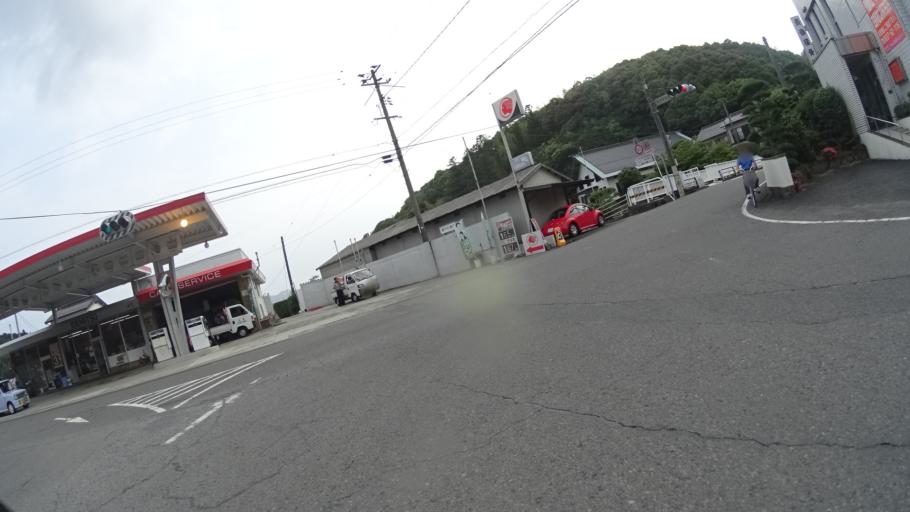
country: JP
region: Yamaguchi
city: Ogori-shimogo
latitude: 34.2184
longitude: 131.2982
